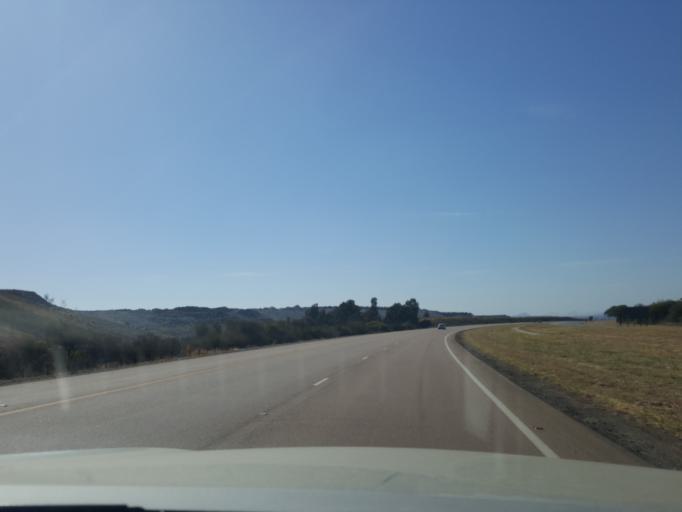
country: ZA
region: North-West
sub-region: Bojanala Platinum District Municipality
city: Rustenburg
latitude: -25.7473
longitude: 27.5083
